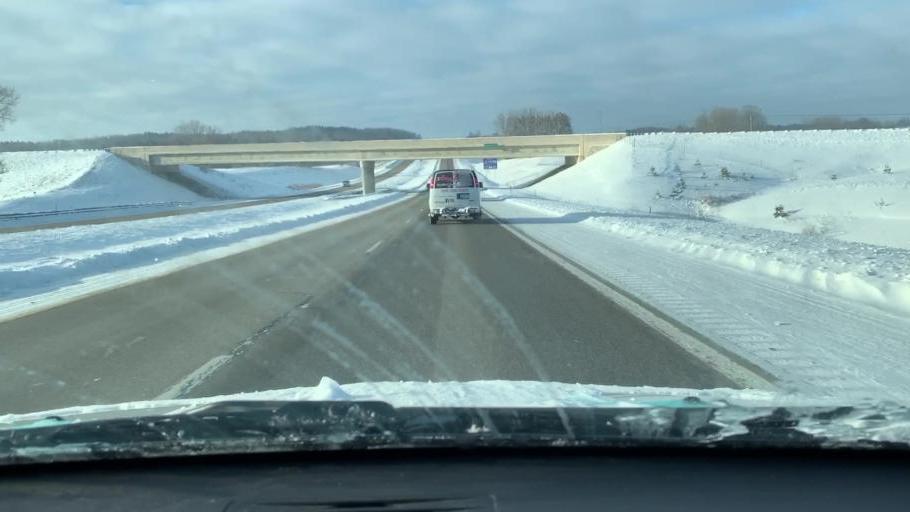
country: US
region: Michigan
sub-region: Wexford County
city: Cadillac
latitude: 44.2326
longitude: -85.3780
